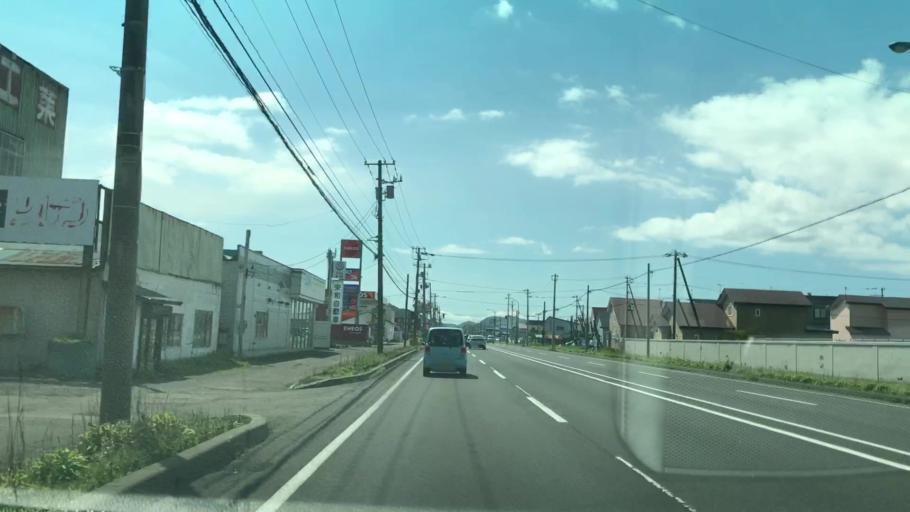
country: JP
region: Hokkaido
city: Muroran
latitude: 42.3692
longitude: 141.0623
